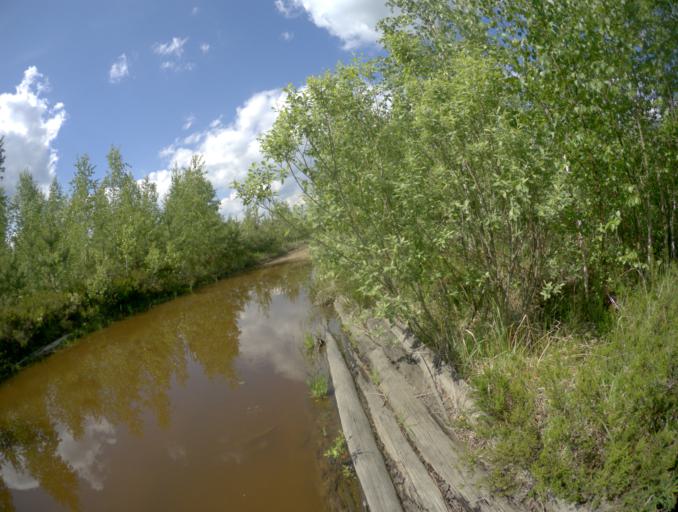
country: RU
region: Vladimir
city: Velikodvorskiy
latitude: 55.2901
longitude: 40.8910
